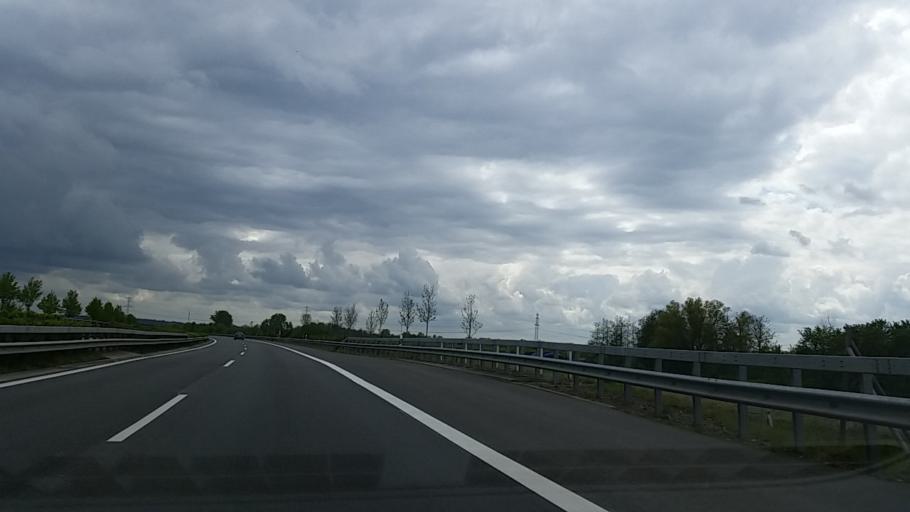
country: DE
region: Lower Saxony
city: Horneburg
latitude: 53.5296
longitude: 9.5794
